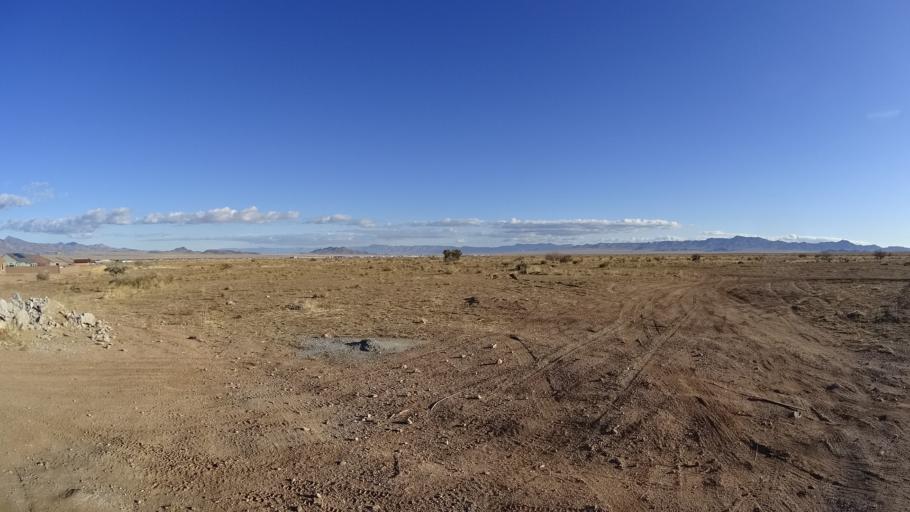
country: US
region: Arizona
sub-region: Mohave County
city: New Kingman-Butler
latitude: 35.2177
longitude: -113.9683
